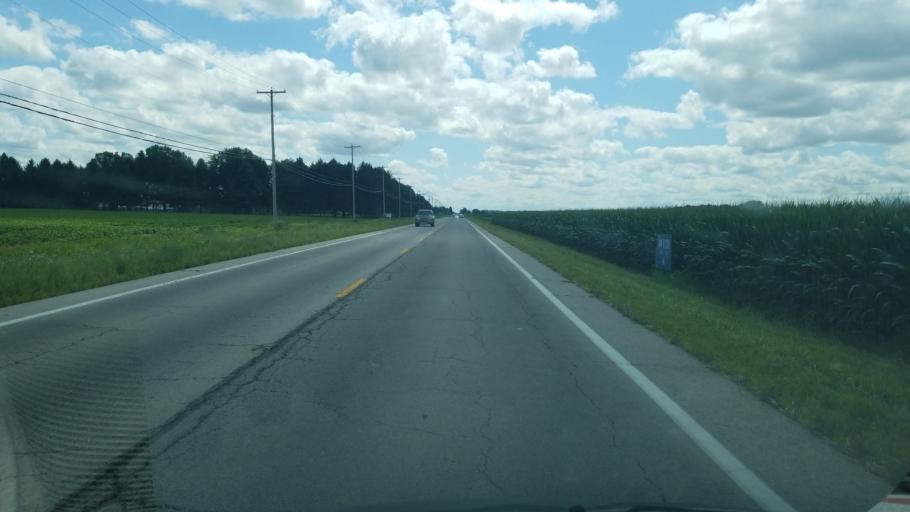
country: US
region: Ohio
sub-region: Henry County
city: Napoleon
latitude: 41.3613
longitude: -84.1201
